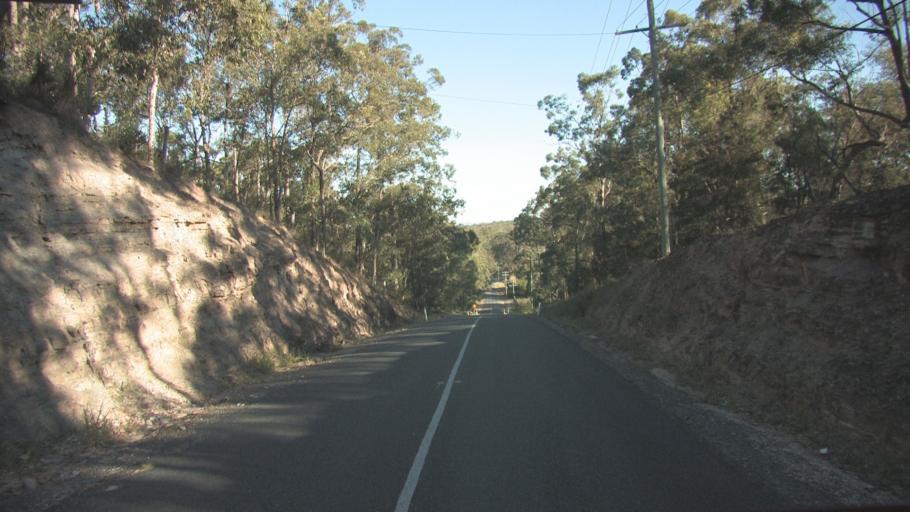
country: AU
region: Queensland
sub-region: Logan
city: Chambers Flat
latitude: -27.7642
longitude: 153.1228
